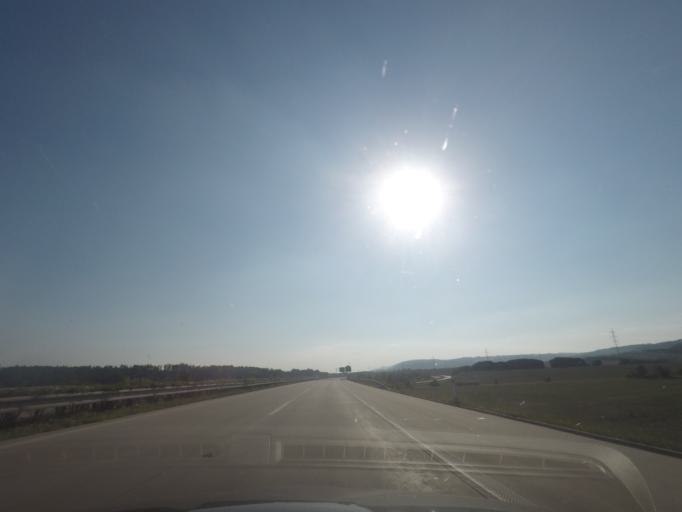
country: CZ
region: Olomoucky
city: Belotin
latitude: 49.5886
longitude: 17.7721
